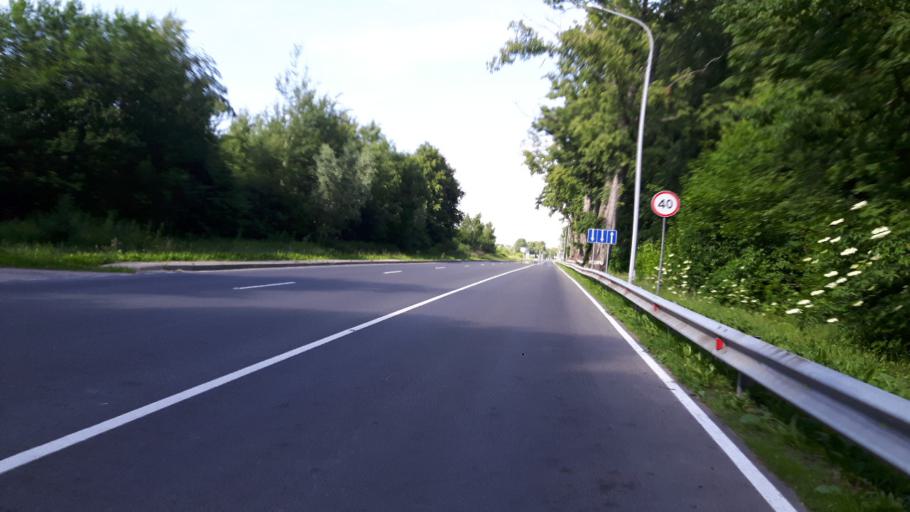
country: RU
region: Kaliningrad
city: Mamonovo
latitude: 54.4475
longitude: 19.9138
